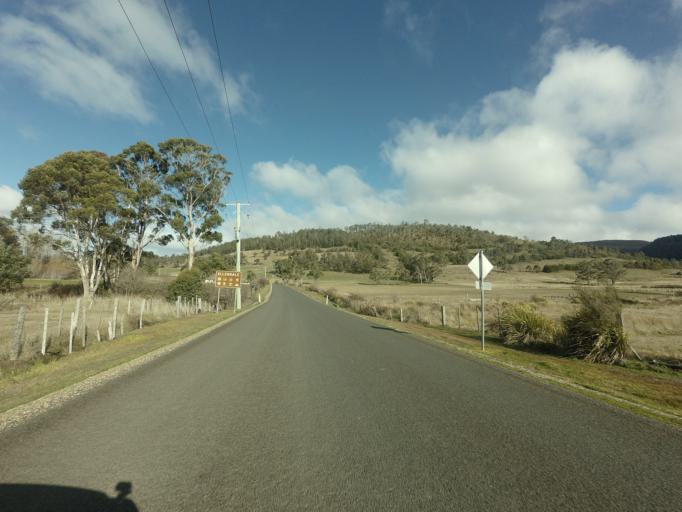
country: AU
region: Tasmania
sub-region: Derwent Valley
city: New Norfolk
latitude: -42.6054
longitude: 146.7059
